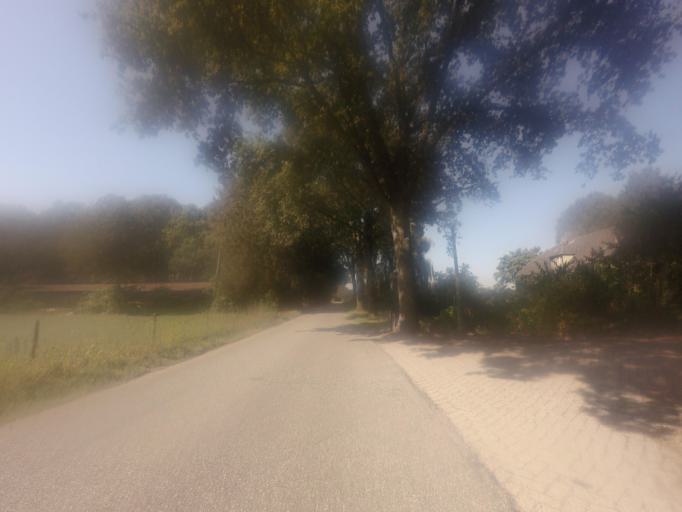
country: NL
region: North Brabant
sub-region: Gemeente Veldhoven
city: Oerle
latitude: 51.4533
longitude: 5.3326
